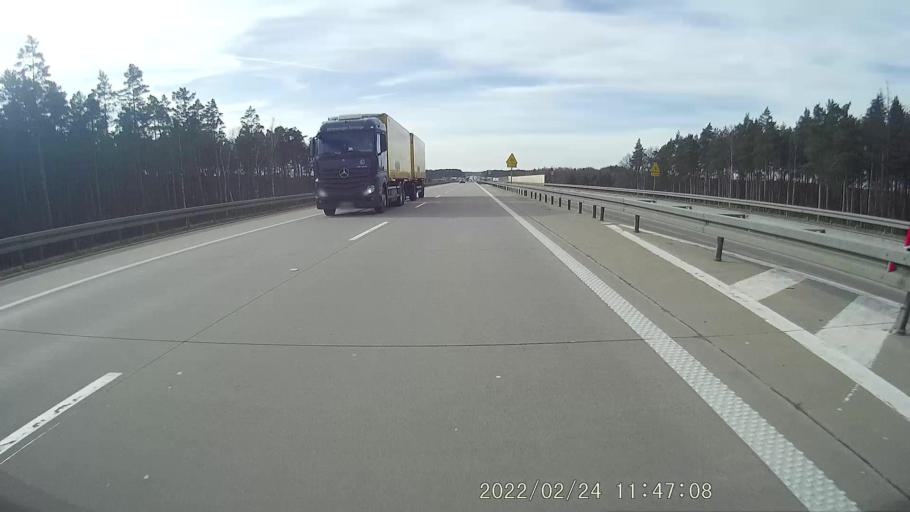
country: PL
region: Lower Silesian Voivodeship
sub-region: Powiat polkowicki
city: Radwanice
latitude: 51.5739
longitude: 15.9488
